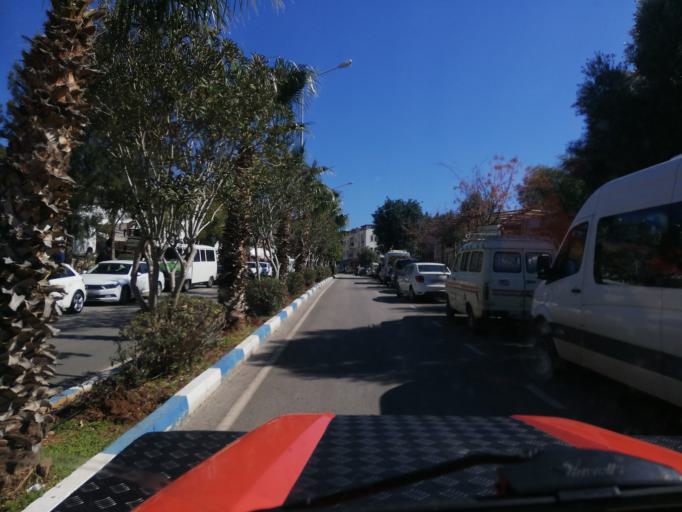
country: TR
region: Antalya
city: Kas
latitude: 36.2025
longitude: 29.6362
